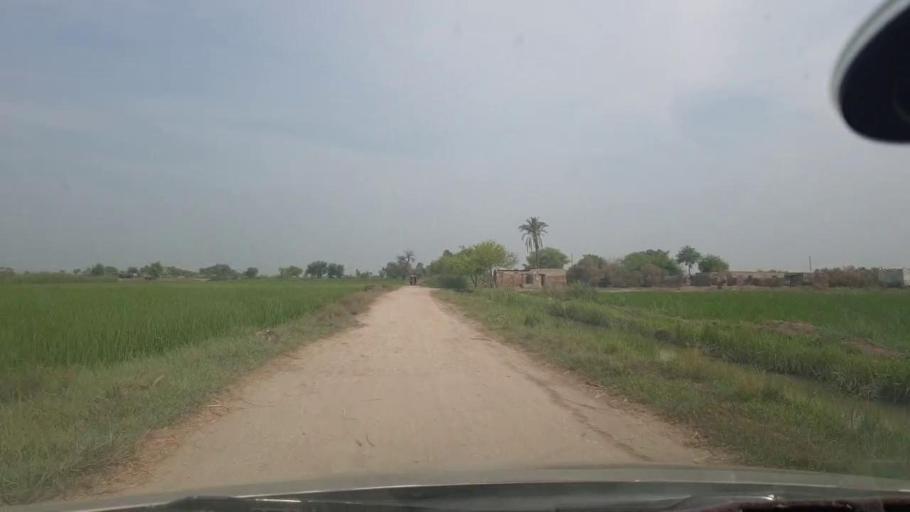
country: PK
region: Sindh
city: Jacobabad
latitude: 28.3127
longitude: 68.4827
